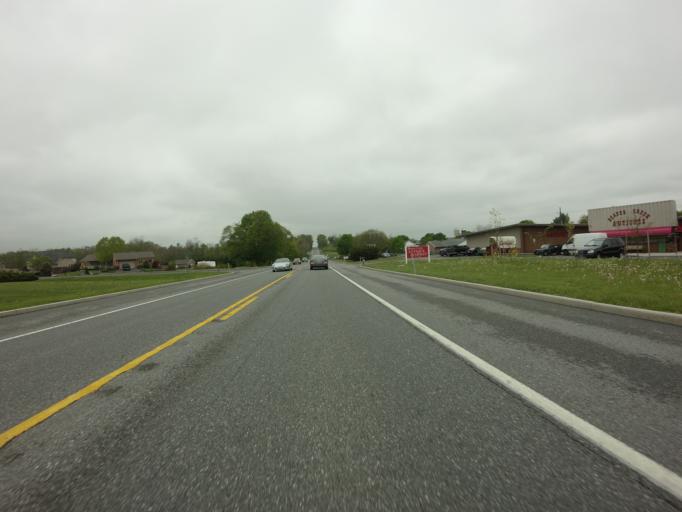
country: US
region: Maryland
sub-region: Washington County
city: Robinwood
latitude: 39.5836
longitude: -77.6643
